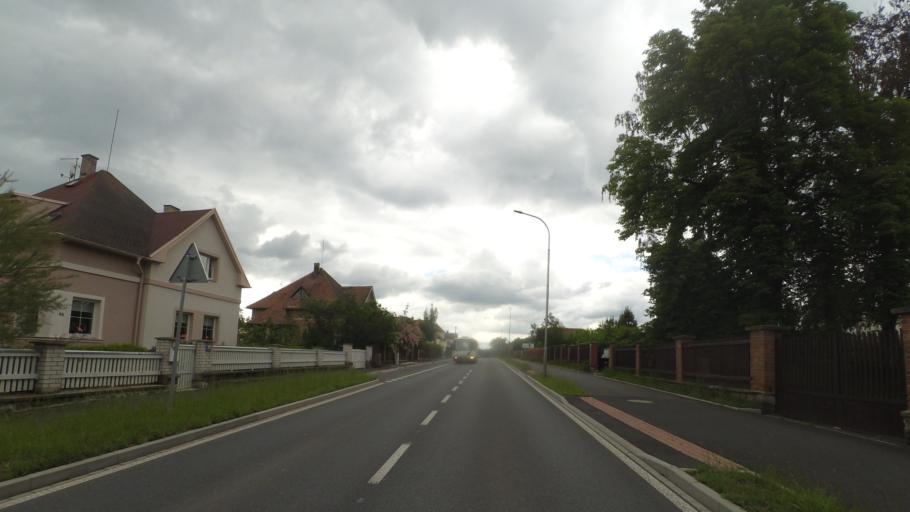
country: CZ
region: Plzensky
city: Horsovsky Tyn
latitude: 49.5319
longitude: 12.9346
